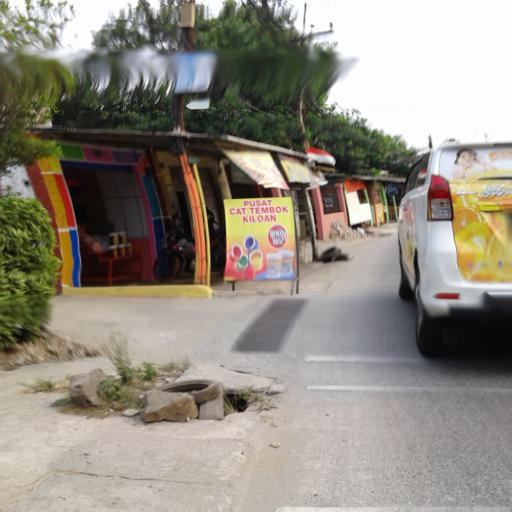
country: ID
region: West Java
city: Sawangan
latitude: -6.3779
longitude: 106.7702
